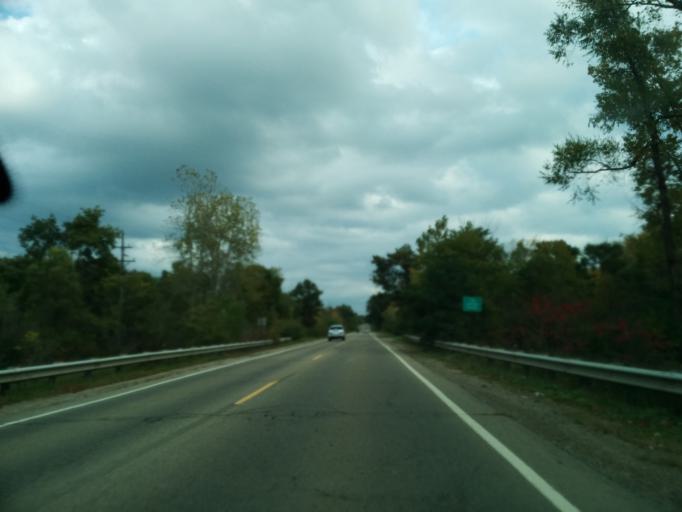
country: US
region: Michigan
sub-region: Oakland County
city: Waterford
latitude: 42.6931
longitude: -83.4998
